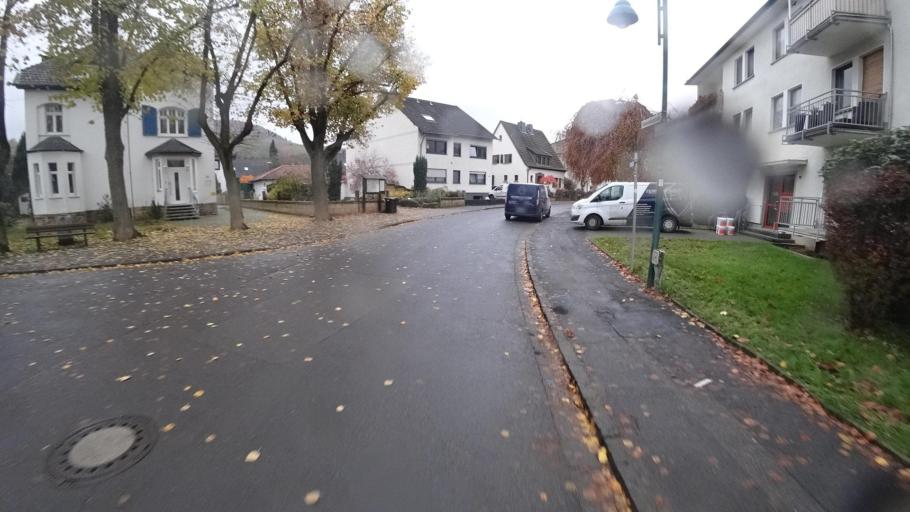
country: DE
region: Rheinland-Pfalz
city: Bad Neuenahr-Ahrweiler
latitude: 50.5377
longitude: 7.0952
